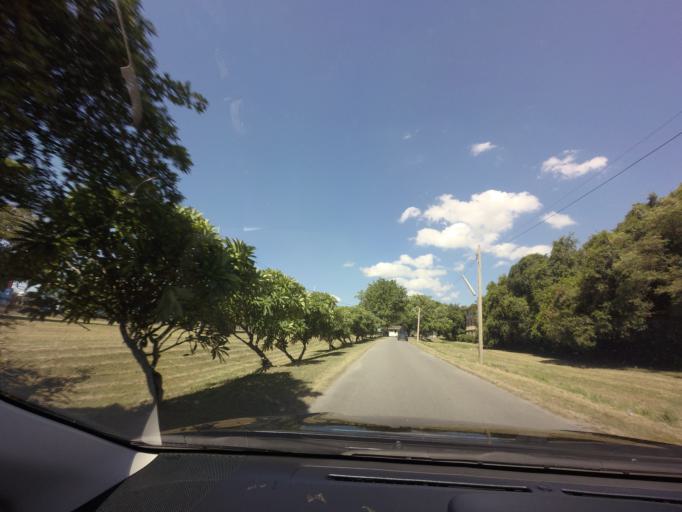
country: TH
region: Chon Buri
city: Bang Lamung
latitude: 13.1059
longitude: 100.9239
